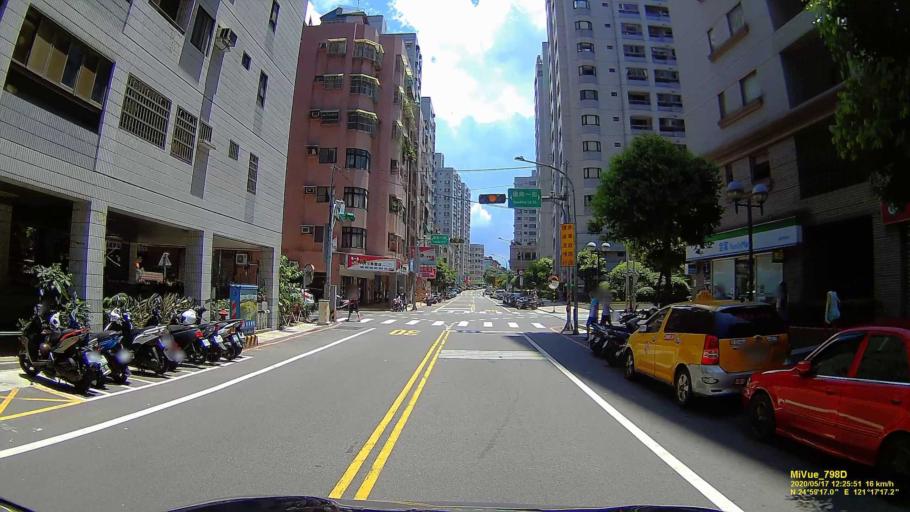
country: TW
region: Taiwan
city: Taoyuan City
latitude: 24.9880
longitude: 121.2881
